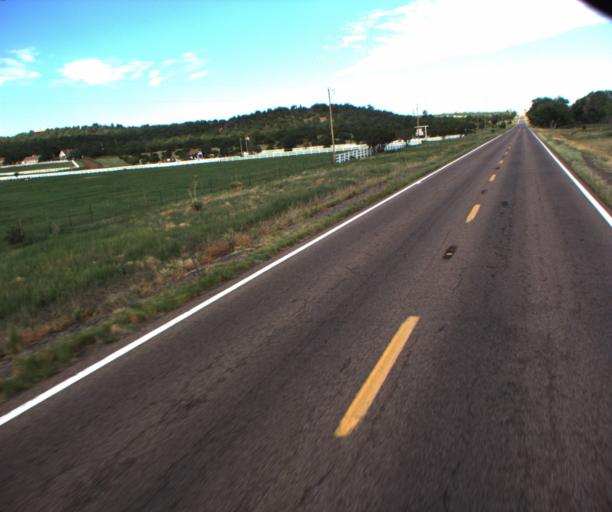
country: US
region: Arizona
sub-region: Navajo County
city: Pinetop-Lakeside
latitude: 34.2716
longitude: -109.6717
